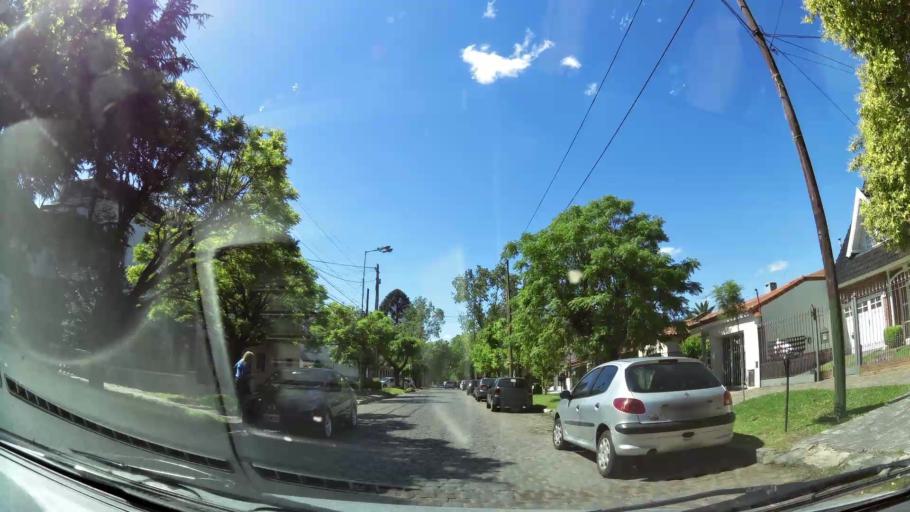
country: AR
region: Buenos Aires
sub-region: Partido de Lomas de Zamora
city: Lomas de Zamora
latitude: -34.7401
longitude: -58.4043
